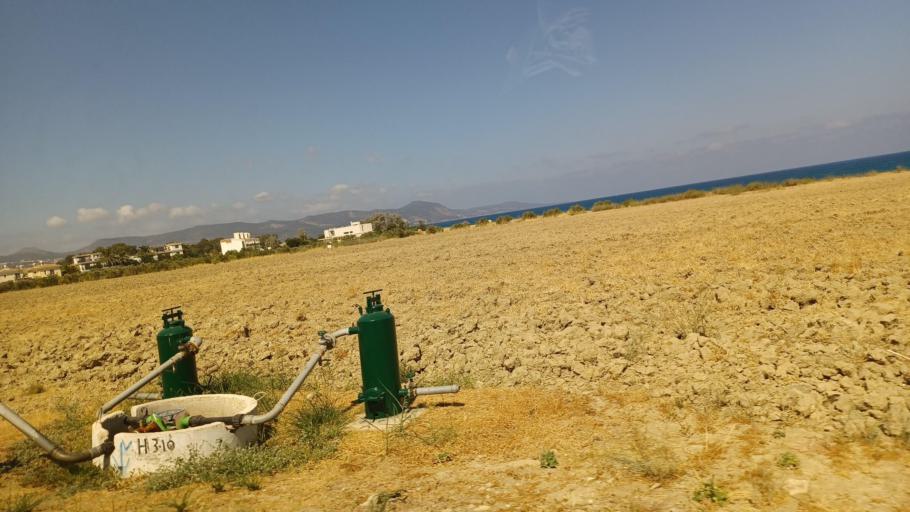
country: CY
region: Pafos
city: Polis
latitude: 35.0433
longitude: 32.4311
